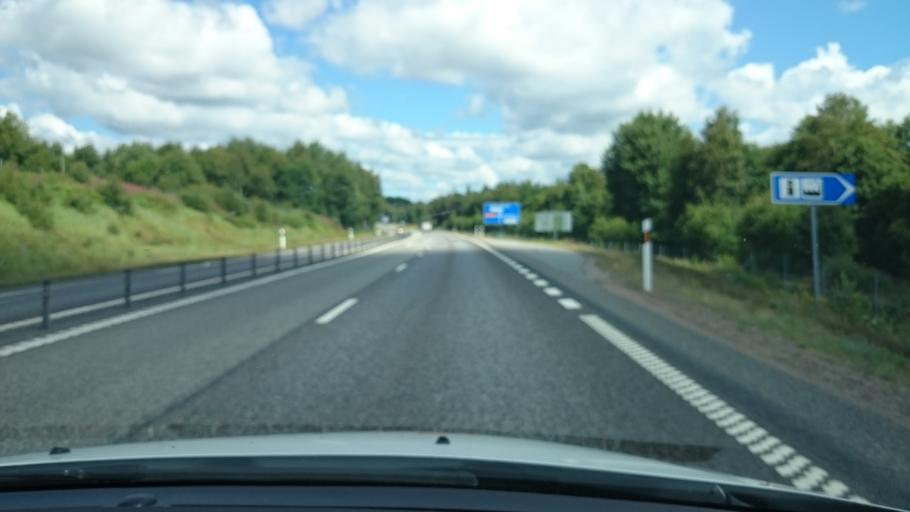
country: SE
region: Halland
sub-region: Hylte Kommun
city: Hyltebruk
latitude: 56.9837
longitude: 13.2118
